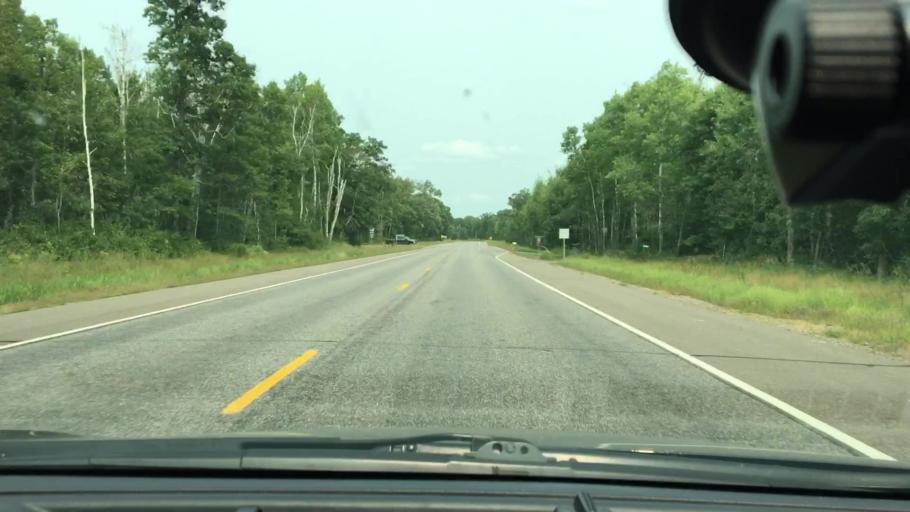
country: US
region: Minnesota
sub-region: Crow Wing County
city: Cross Lake
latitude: 46.6933
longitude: -94.0732
